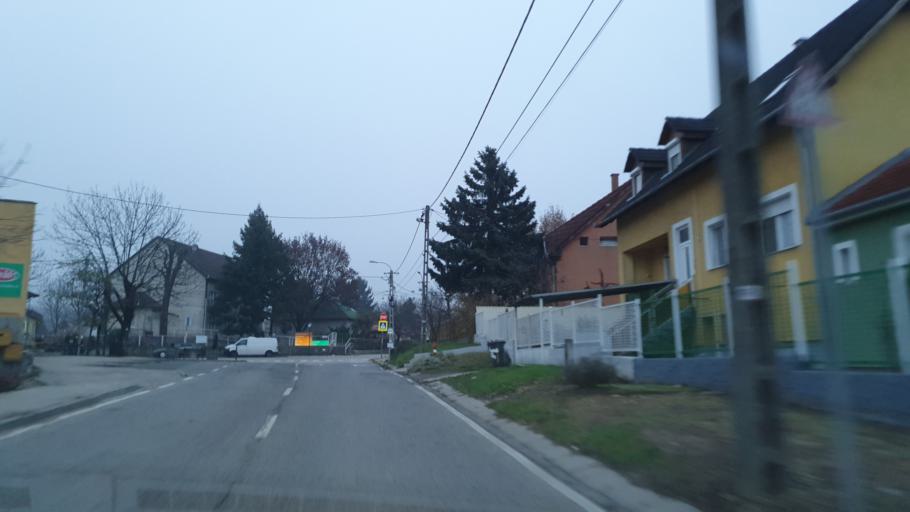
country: HU
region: Pest
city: Csomor
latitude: 47.5425
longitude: 19.2250
